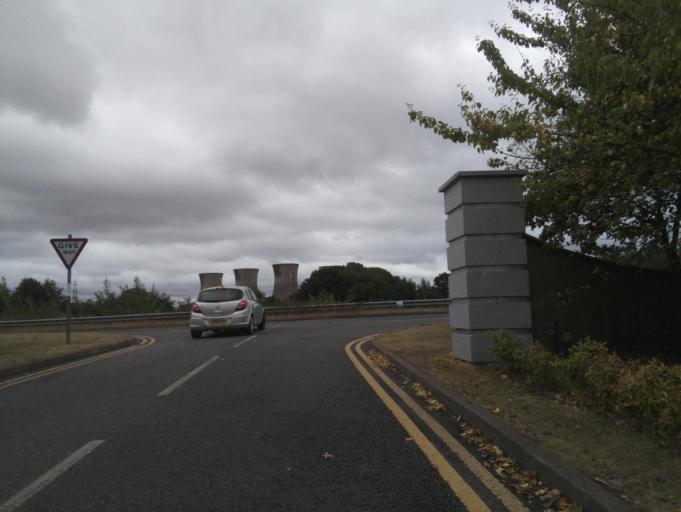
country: GB
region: England
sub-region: Derbyshire
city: Findern
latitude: 52.8607
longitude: -1.5532
